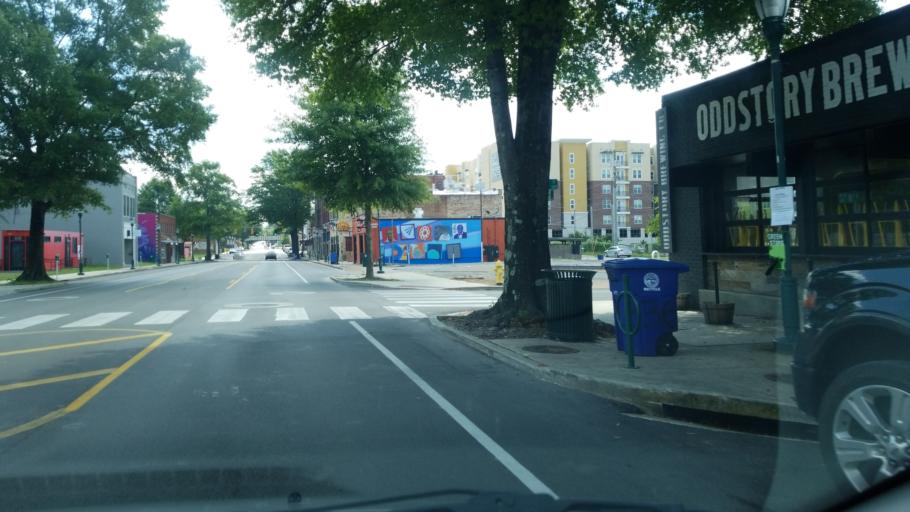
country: US
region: Tennessee
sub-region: Hamilton County
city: Chattanooga
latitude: 35.0442
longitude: -85.3042
